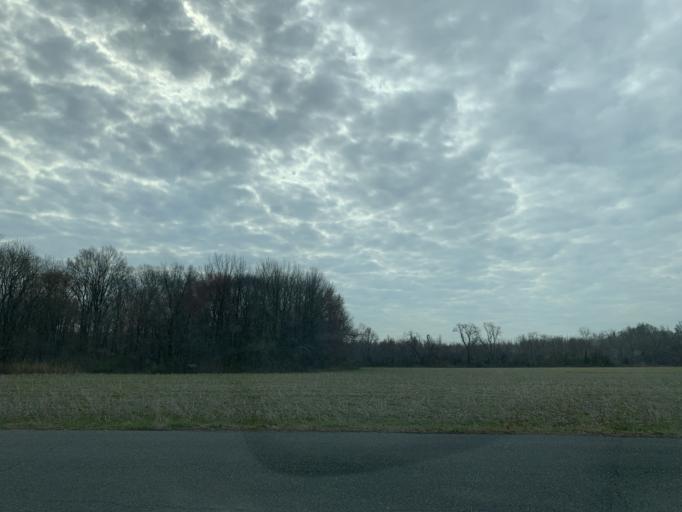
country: US
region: Maryland
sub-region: Baltimore County
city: Edgemere
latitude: 39.2602
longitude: -76.4286
